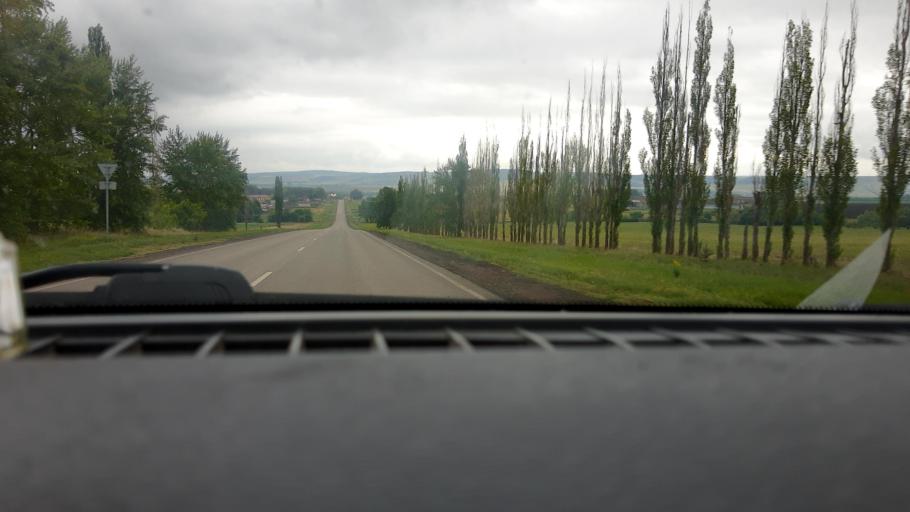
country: RU
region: Bashkortostan
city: Serafimovskiy
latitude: 54.4428
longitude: 53.9642
